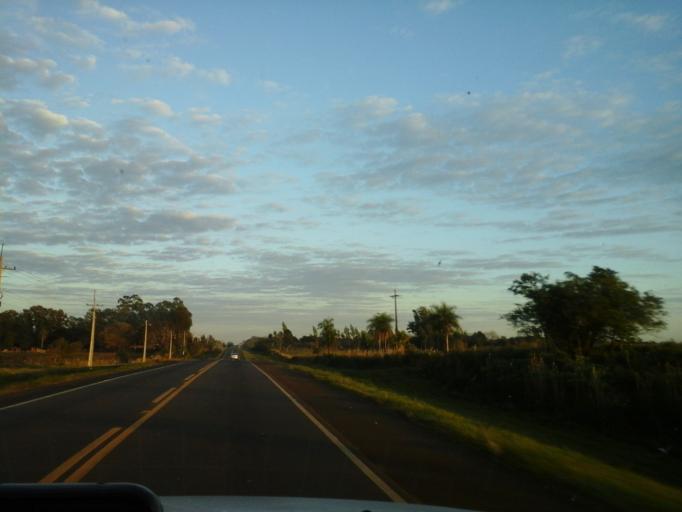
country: PY
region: Misiones
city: San Patricio
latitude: -27.0314
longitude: -56.6862
